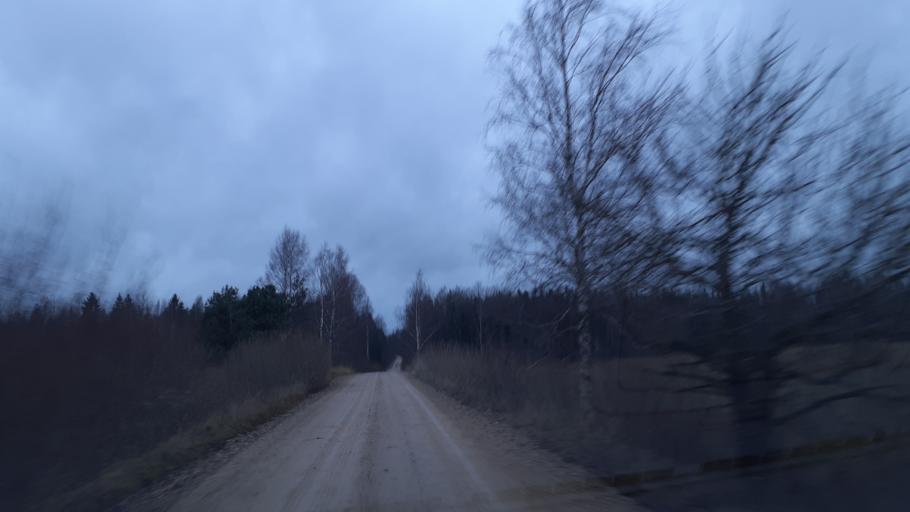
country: LV
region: Kuldigas Rajons
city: Kuldiga
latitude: 57.0479
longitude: 22.1293
